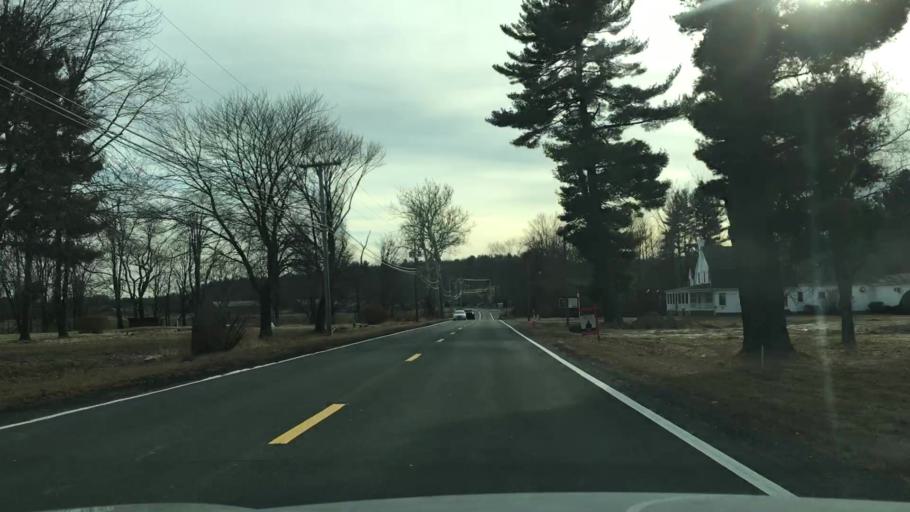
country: US
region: Massachusetts
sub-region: Hampden County
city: Southwick
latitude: 42.0807
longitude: -72.7676
